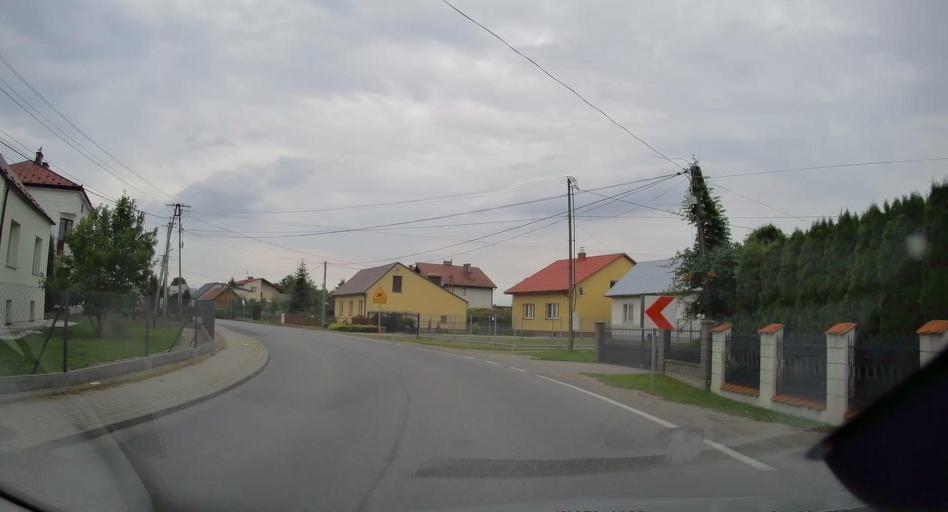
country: PL
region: Lesser Poland Voivodeship
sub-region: Powiat tarnowski
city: Wierzchoslawice
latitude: 49.9947
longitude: 20.8474
